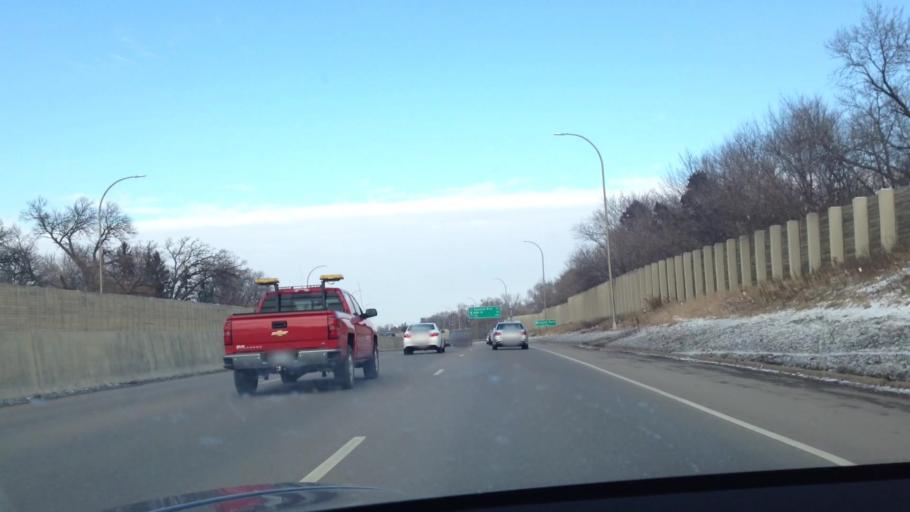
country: US
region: Minnesota
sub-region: Hennepin County
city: Saint Louis Park
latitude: 44.9190
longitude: -93.3496
